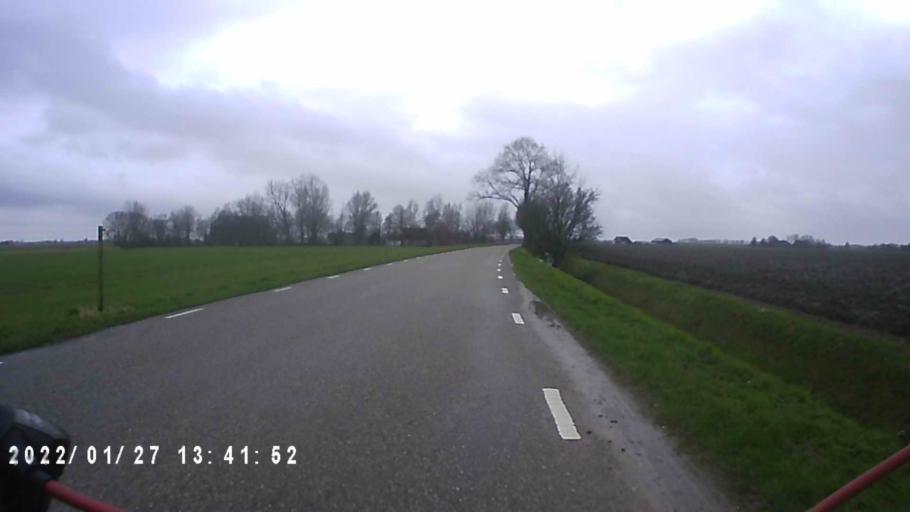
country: NL
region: Friesland
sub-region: Gemeente Kollumerland en Nieuwkruisland
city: Kollum
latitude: 53.3015
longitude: 6.2129
